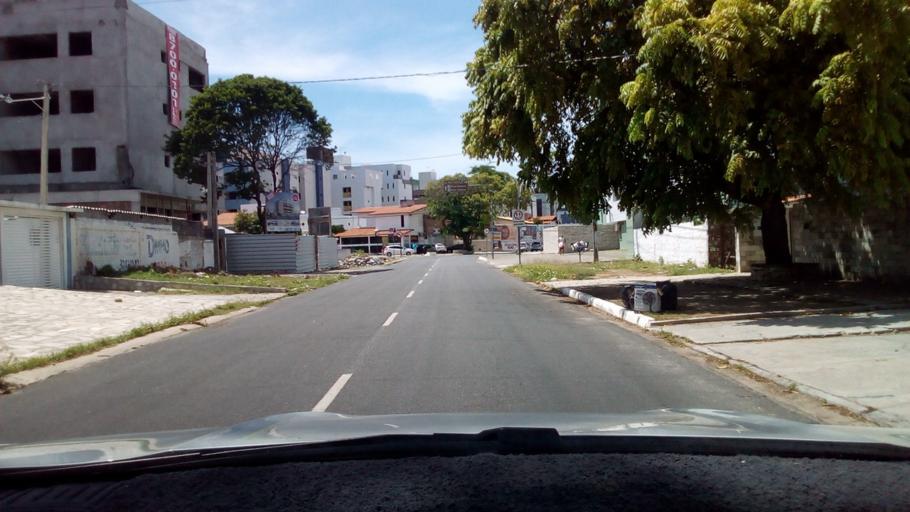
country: BR
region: Paraiba
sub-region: Joao Pessoa
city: Joao Pessoa
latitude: -7.0743
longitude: -34.8319
